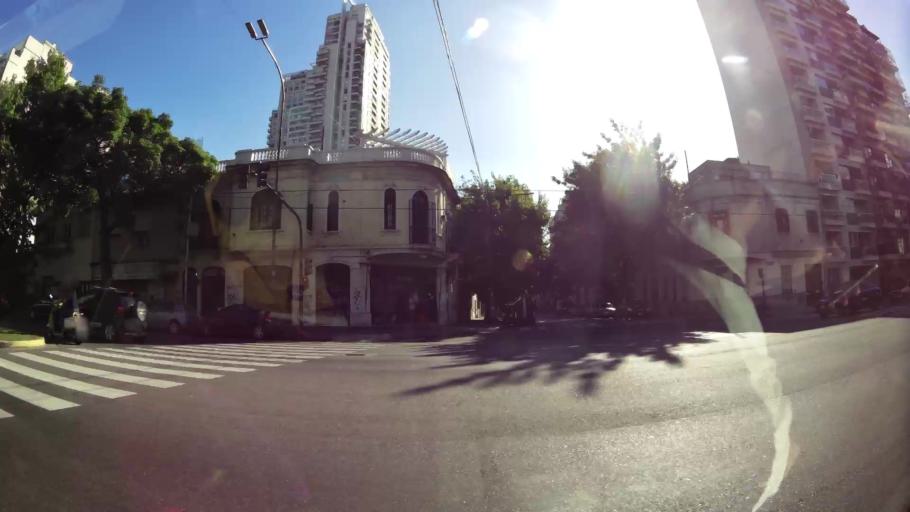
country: AR
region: Buenos Aires F.D.
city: Colegiales
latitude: -34.6109
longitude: -58.4429
